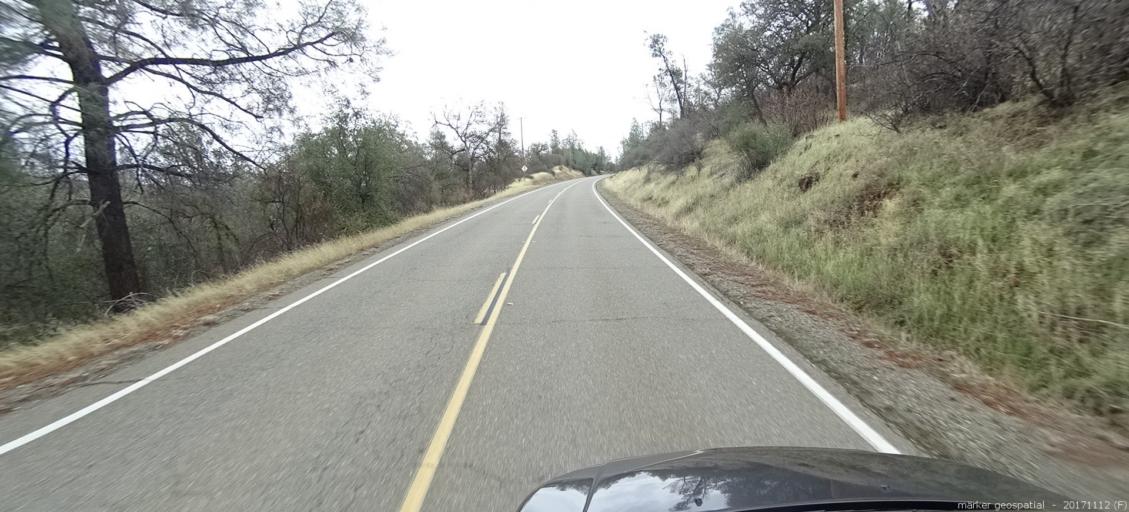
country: US
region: California
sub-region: Shasta County
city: Palo Cedro
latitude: 40.4883
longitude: -122.1331
